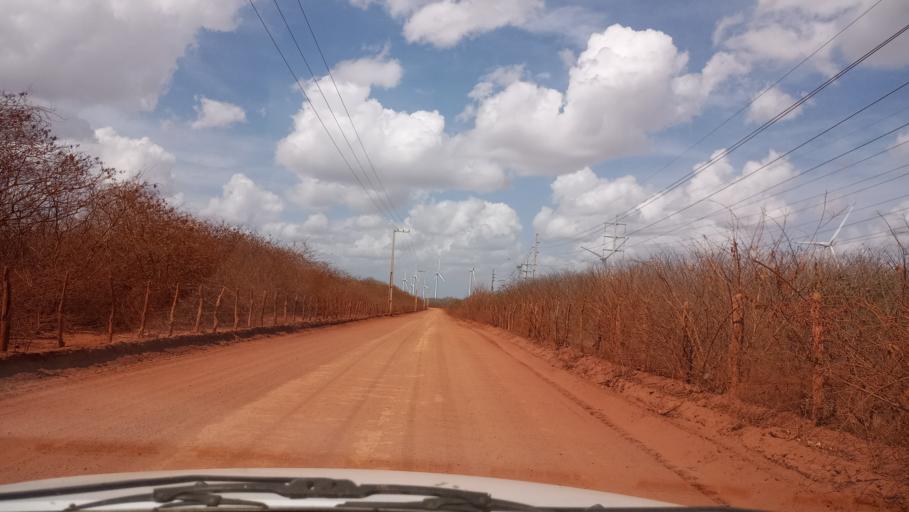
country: BR
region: Rio Grande do Norte
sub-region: Joao Camara
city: Joao Camara
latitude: -5.3651
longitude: -35.8379
